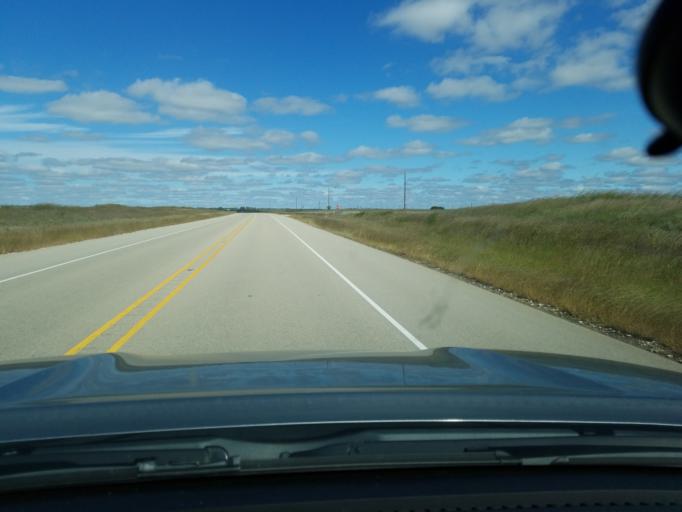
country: US
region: Texas
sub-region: Hamilton County
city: Hamilton
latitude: 31.6285
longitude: -98.1536
